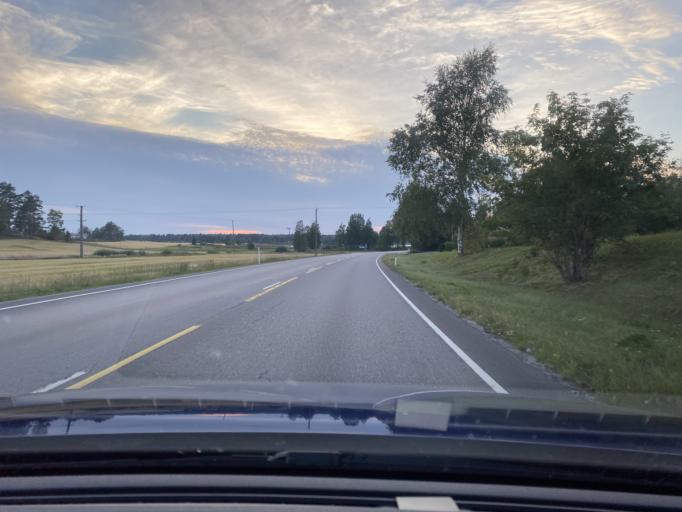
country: FI
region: Satakunta
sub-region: Pohjois-Satakunta
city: Kankaanpaeae
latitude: 61.7849
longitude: 22.4245
